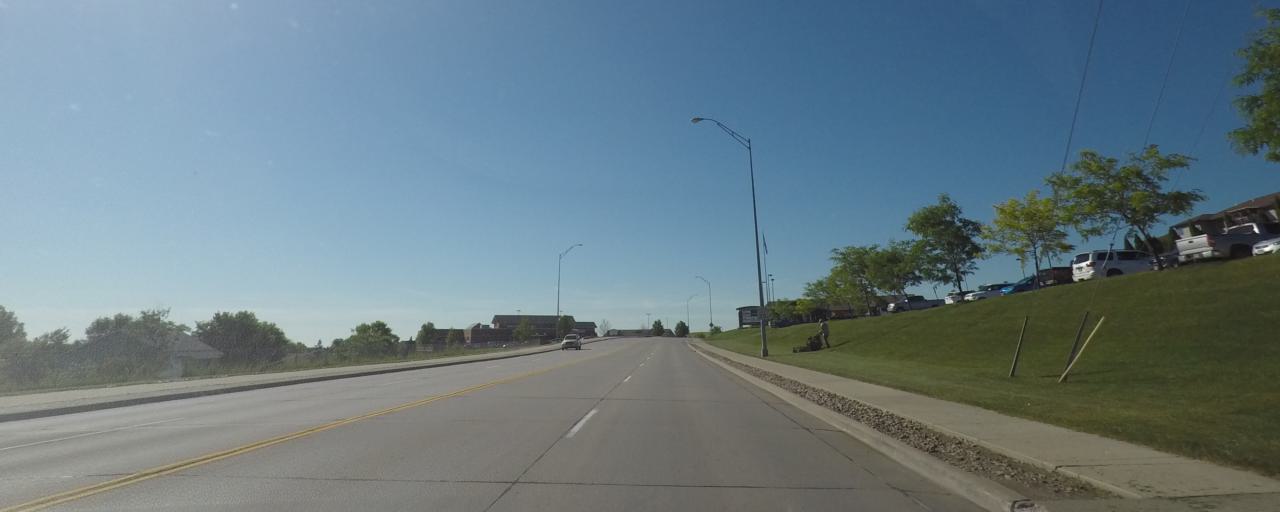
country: US
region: South Dakota
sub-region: Pennington County
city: Rapid City
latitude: 44.0458
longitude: -103.2209
